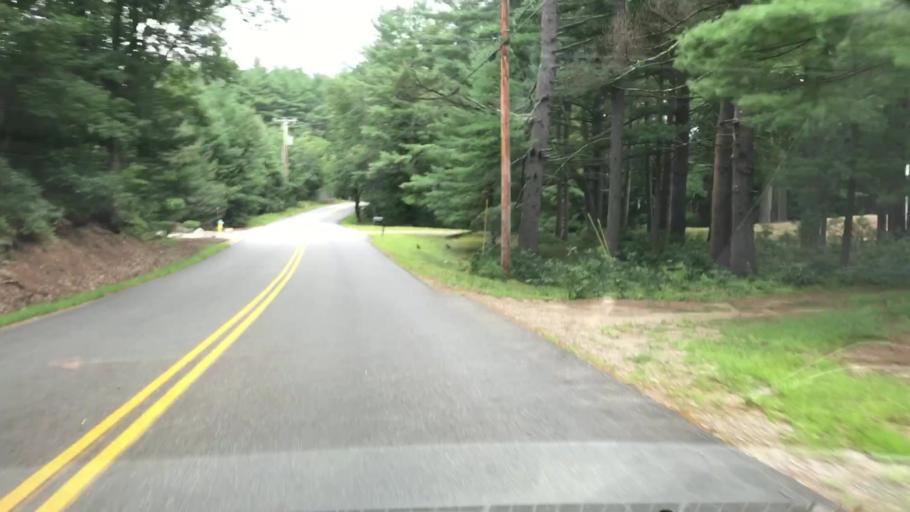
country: US
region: New Hampshire
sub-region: Hillsborough County
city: Milford
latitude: 42.8167
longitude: -71.5975
